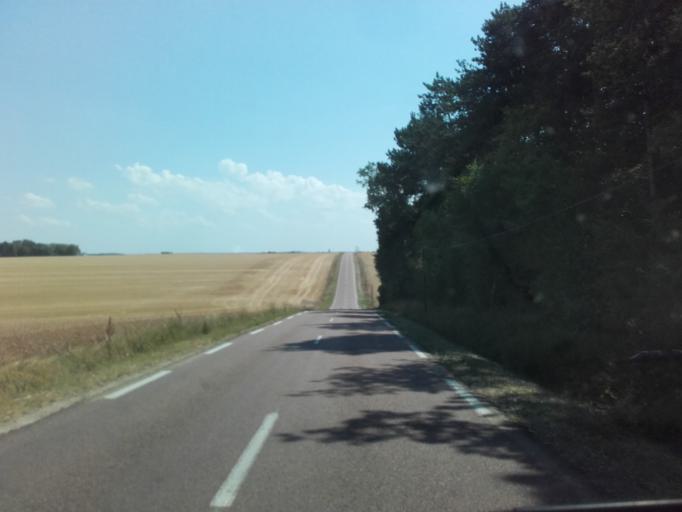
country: FR
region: Bourgogne
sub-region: Departement de l'Yonne
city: Joux-la-Ville
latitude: 47.6920
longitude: 3.8648
